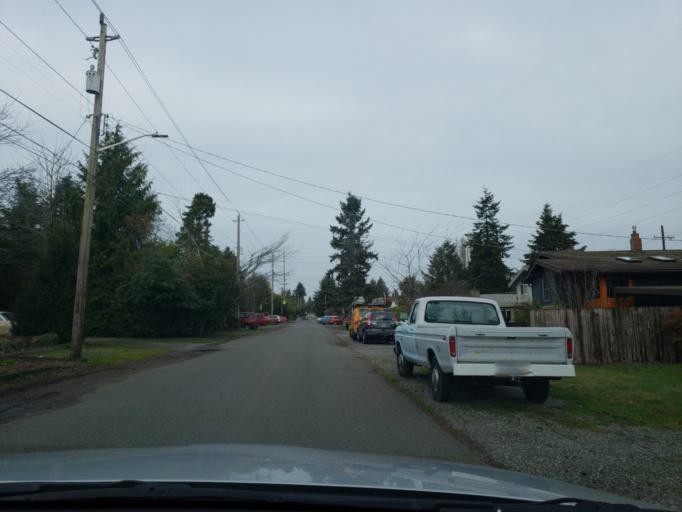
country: US
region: Washington
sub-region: King County
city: Shoreline
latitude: 47.6963
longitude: -122.3513
